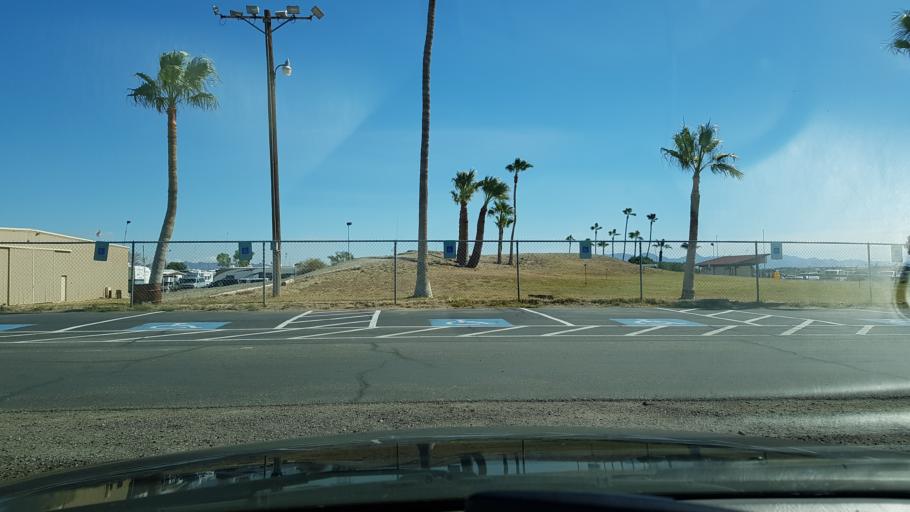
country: US
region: Arizona
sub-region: Yuma County
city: Yuma
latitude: 32.6711
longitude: -114.5928
